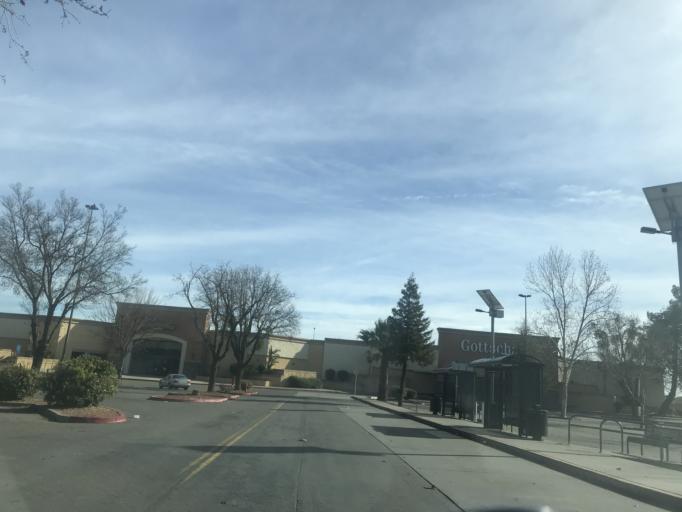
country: US
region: California
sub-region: Yolo County
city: Woodland
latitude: 38.6599
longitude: -121.7643
